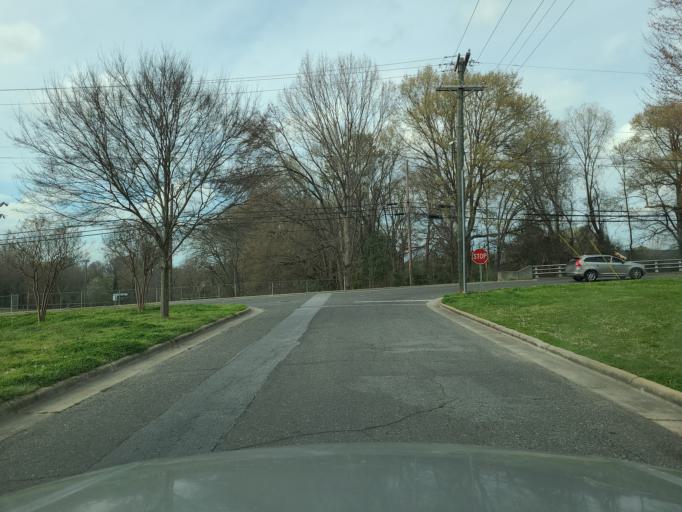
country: US
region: North Carolina
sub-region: Cleveland County
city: Shelby
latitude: 35.2932
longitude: -81.5435
